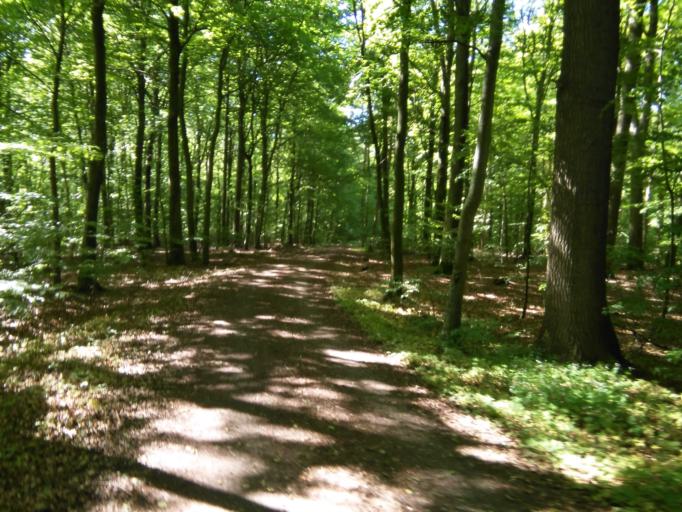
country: DK
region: Central Jutland
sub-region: Arhus Kommune
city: Malling
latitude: 56.0212
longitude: 10.1692
